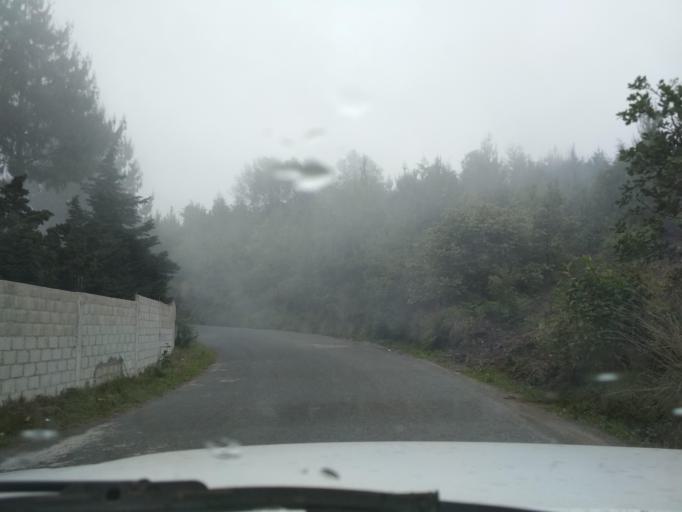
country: MX
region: Veracruz
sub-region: Mariano Escobedo
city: Loma Grande
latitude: 18.9335
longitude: -97.2203
